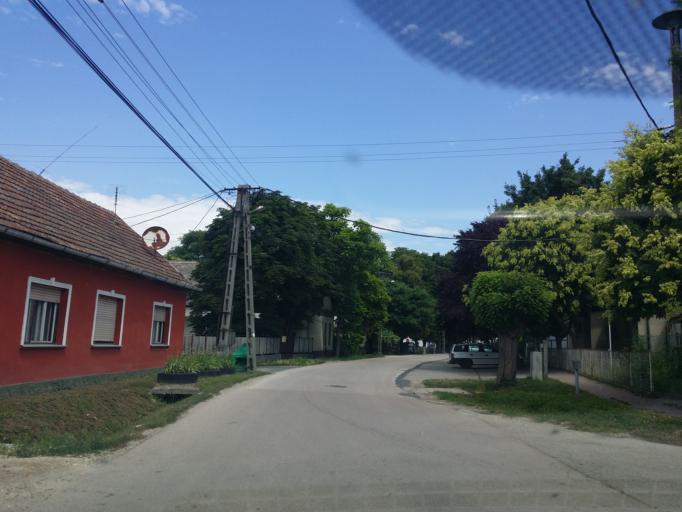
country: HU
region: Pest
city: Domsod
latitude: 47.0937
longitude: 19.0028
